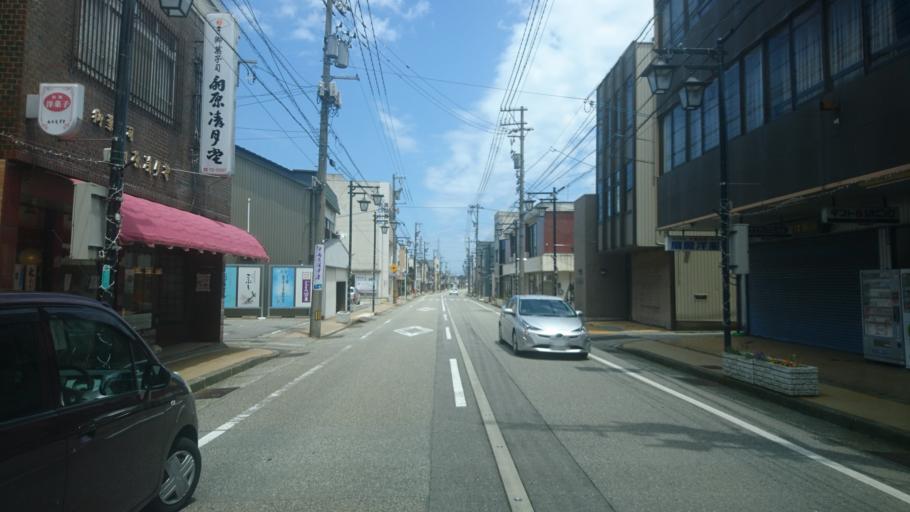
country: JP
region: Toyama
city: Nyuzen
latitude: 36.9402
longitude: 137.5018
